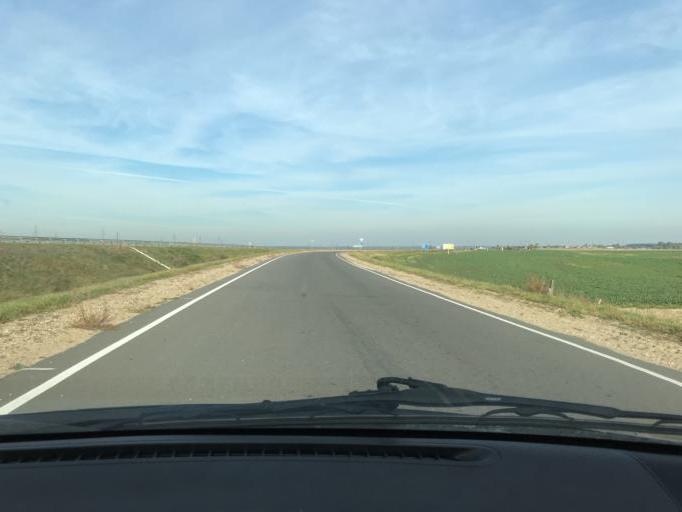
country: BY
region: Brest
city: Asnyezhytsy
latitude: 52.1851
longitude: 26.0846
